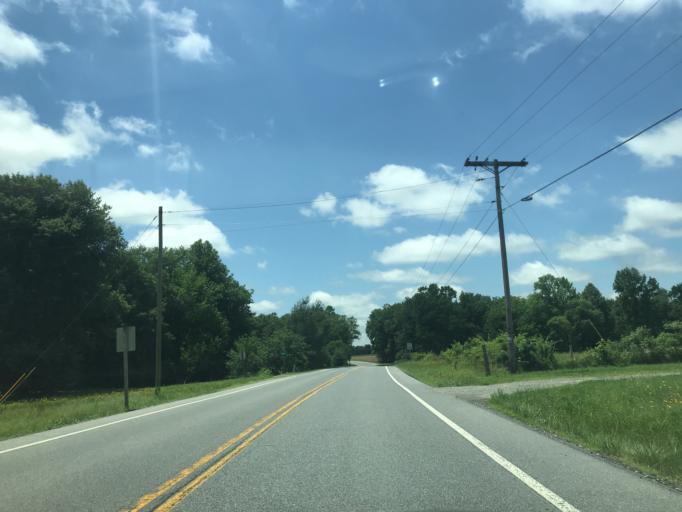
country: US
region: Maryland
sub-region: Caroline County
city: Federalsburg
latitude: 38.7345
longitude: -75.7273
